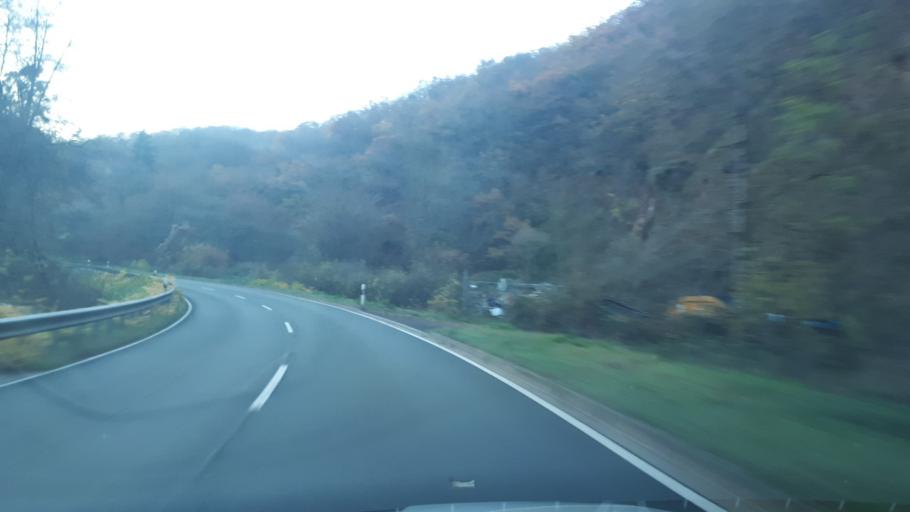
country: DE
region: Rheinland-Pfalz
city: Alf
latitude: 50.0640
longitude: 7.0962
